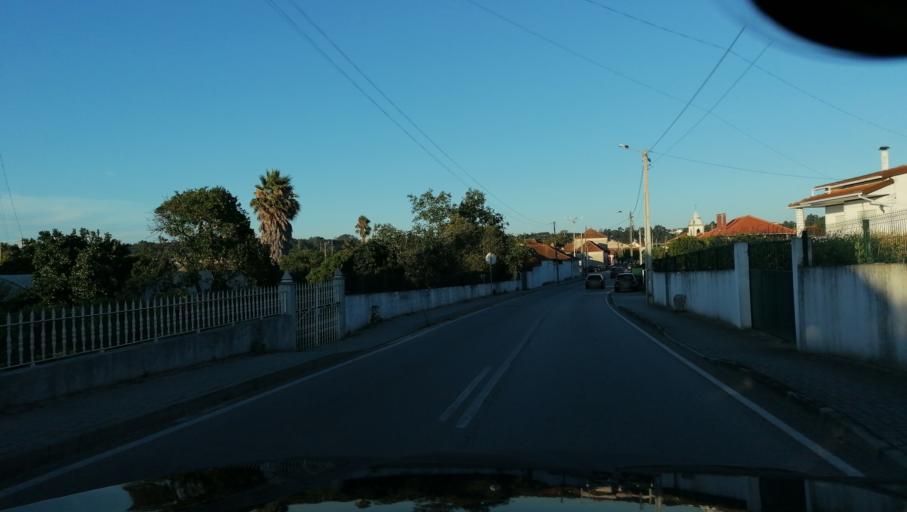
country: PT
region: Aveiro
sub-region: Oliveira do Bairro
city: Oia
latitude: 40.5467
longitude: -8.5100
